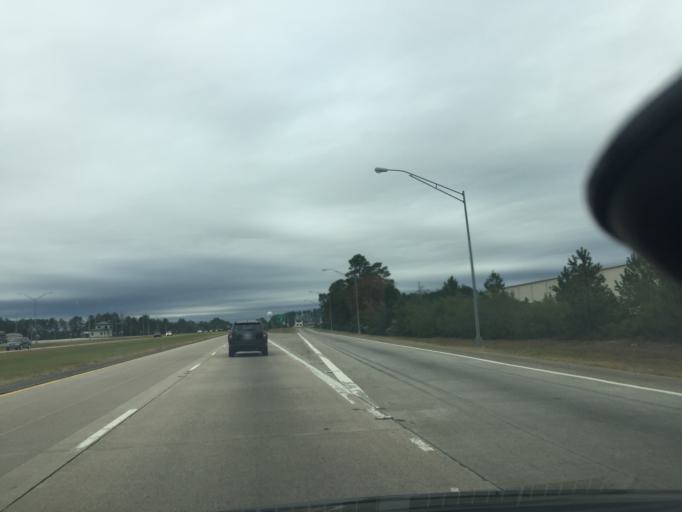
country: US
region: Georgia
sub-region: Chatham County
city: Bloomingdale
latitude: 32.1661
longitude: -81.4400
